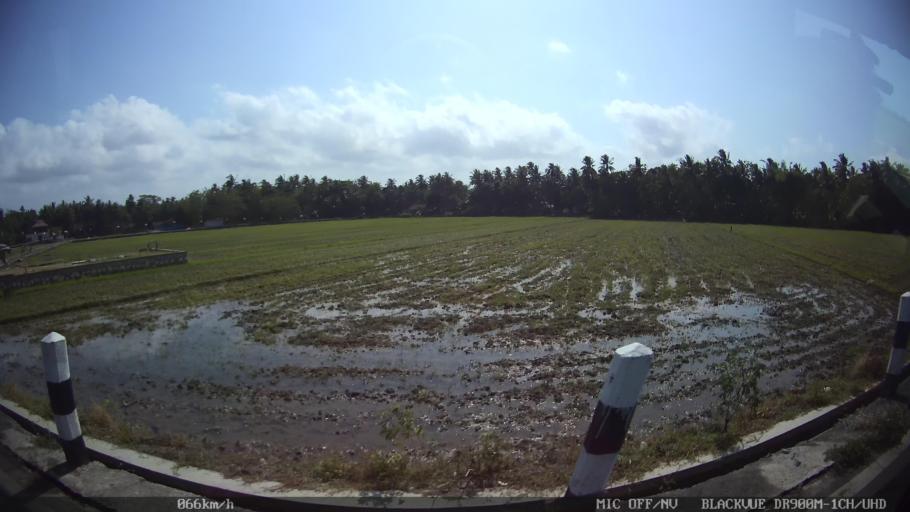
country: ID
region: Daerah Istimewa Yogyakarta
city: Srandakan
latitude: -7.9277
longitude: 110.1902
